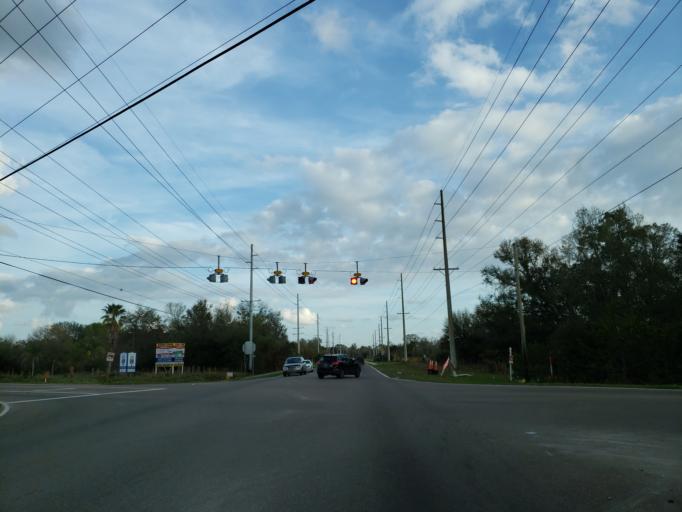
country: US
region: Florida
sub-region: Hillsborough County
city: Riverview
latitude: 27.8217
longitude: -82.2982
